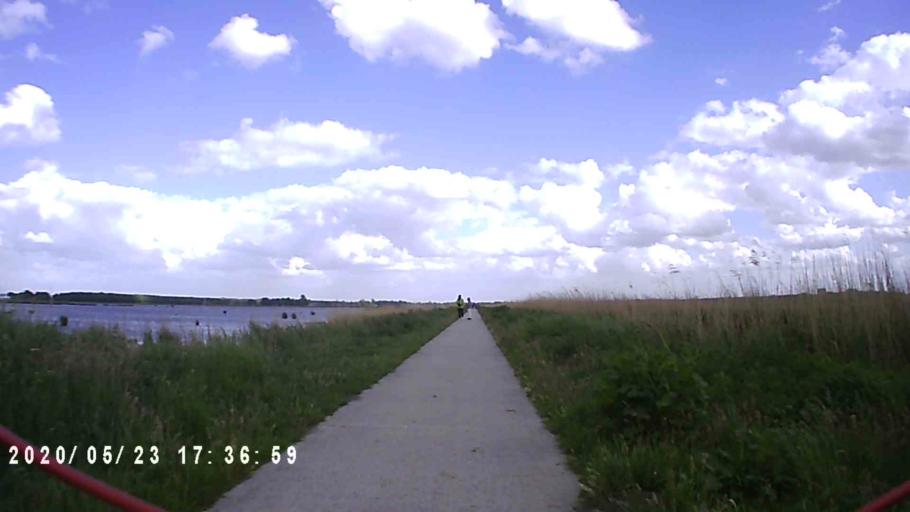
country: NL
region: Groningen
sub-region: Gemeente Slochteren
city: Slochteren
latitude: 53.2456
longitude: 6.7782
